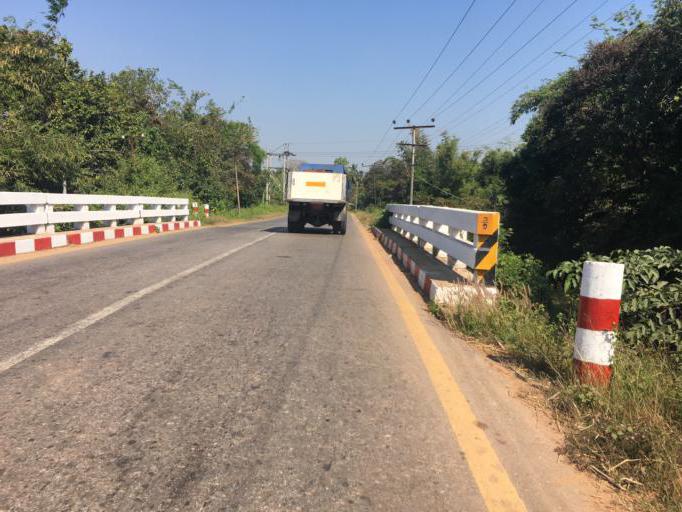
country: MM
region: Mon
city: Mawlamyine
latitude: 16.4241
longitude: 97.6978
